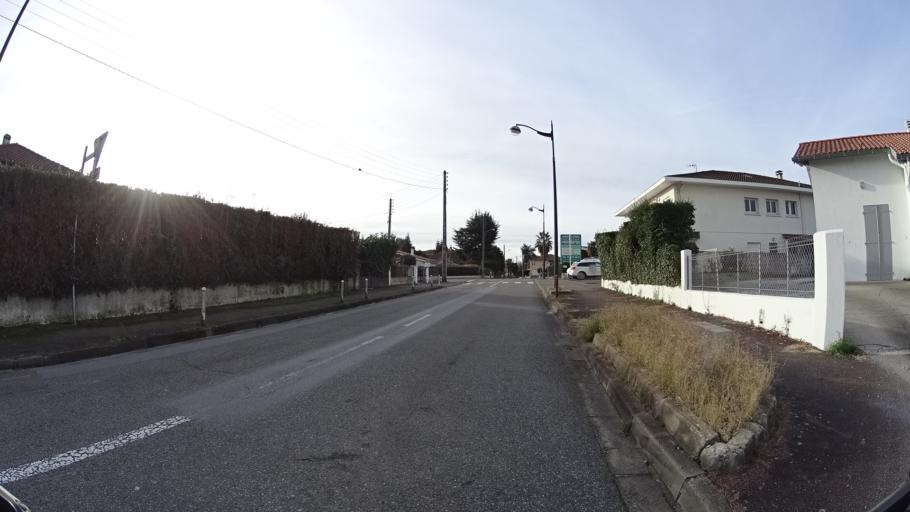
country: FR
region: Aquitaine
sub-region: Departement des Landes
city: Saint-Paul-les-Dax
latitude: 43.7292
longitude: -1.0501
